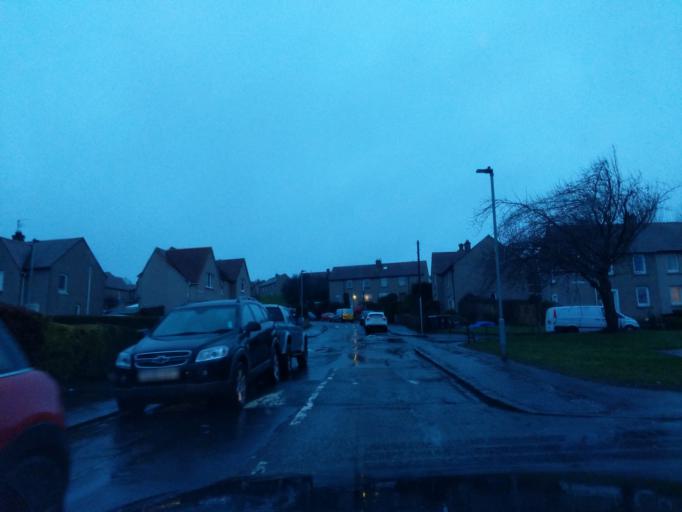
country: GB
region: Scotland
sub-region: Edinburgh
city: Colinton
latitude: 55.9583
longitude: -3.2920
